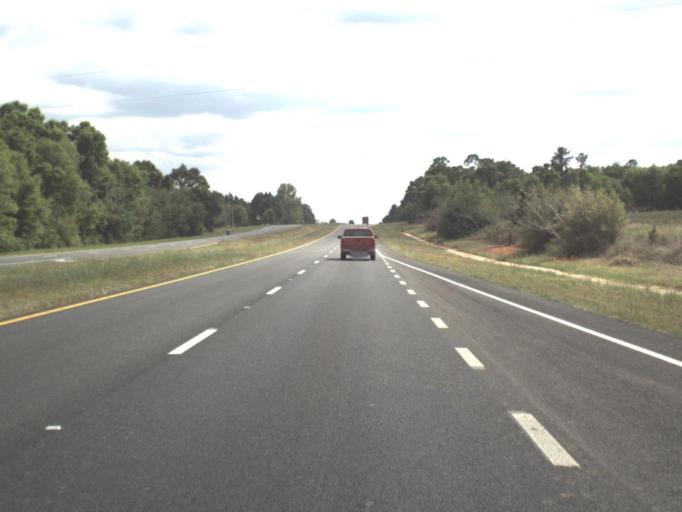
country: US
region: Florida
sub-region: Escambia County
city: Century
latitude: 30.9128
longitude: -87.3154
